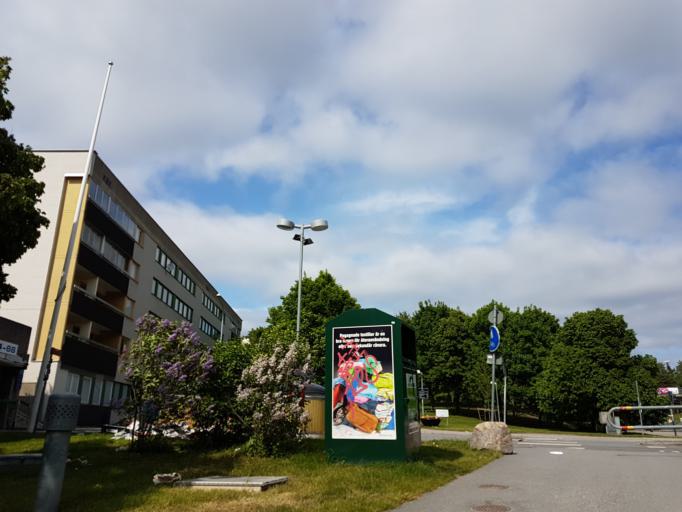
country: SE
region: Stockholm
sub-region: Sundbybergs Kommun
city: Sundbyberg
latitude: 59.3768
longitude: 17.9554
